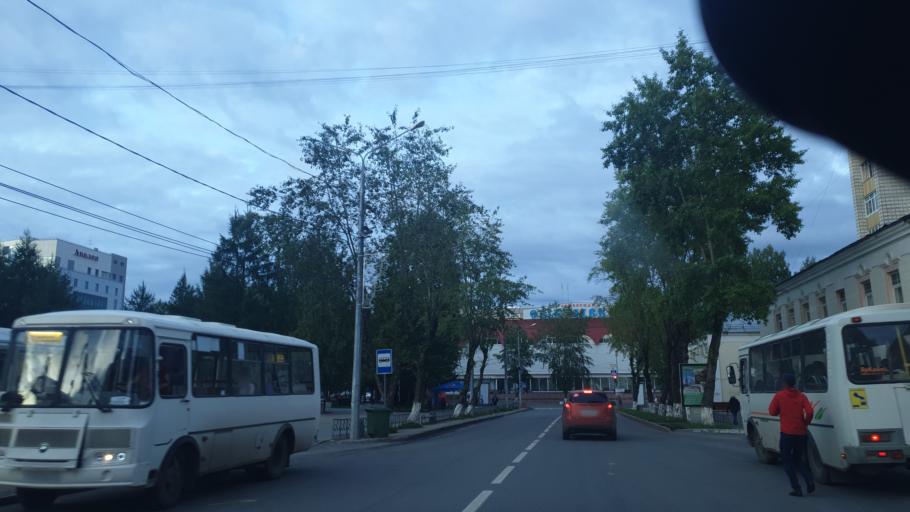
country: RU
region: Komi Republic
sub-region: Syktyvdinskiy Rayon
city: Syktyvkar
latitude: 61.6672
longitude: 50.8301
